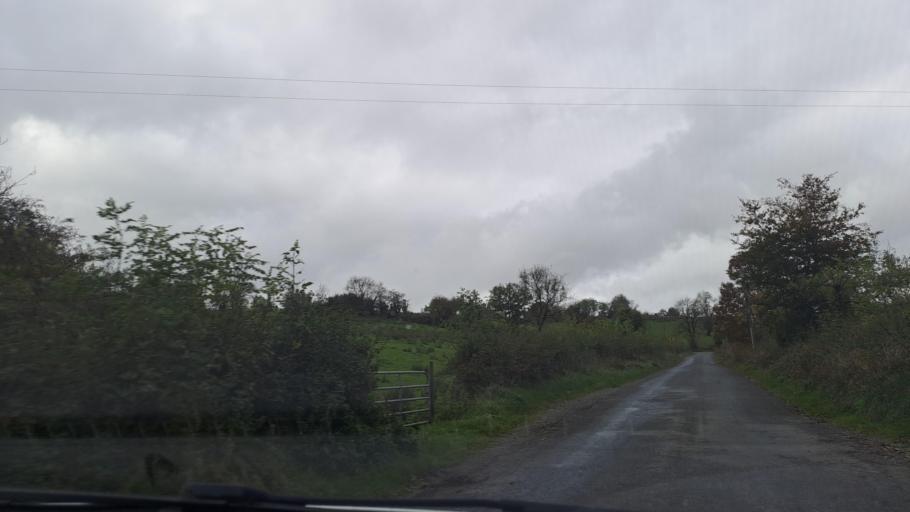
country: IE
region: Ulster
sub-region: An Cabhan
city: Bailieborough
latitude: 53.9339
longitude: -6.9195
